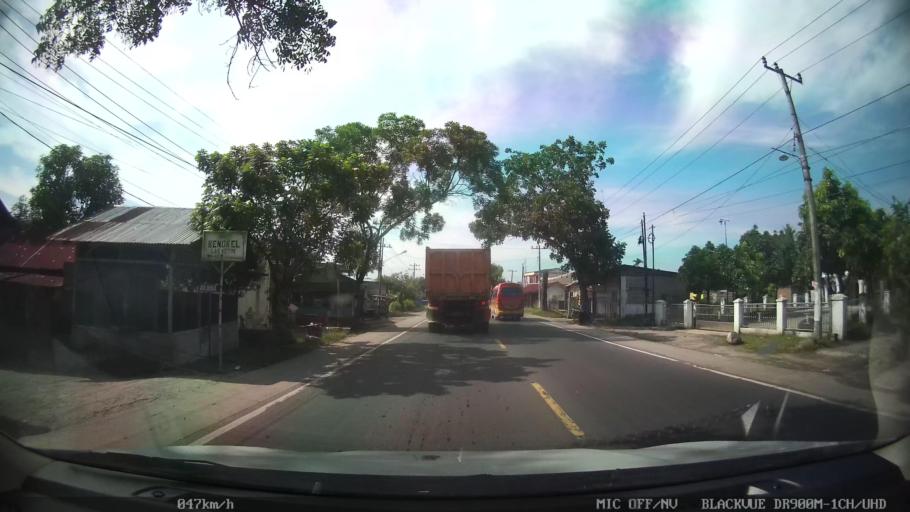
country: ID
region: North Sumatra
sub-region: Kabupaten Langkat
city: Stabat
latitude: 3.7197
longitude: 98.5032
